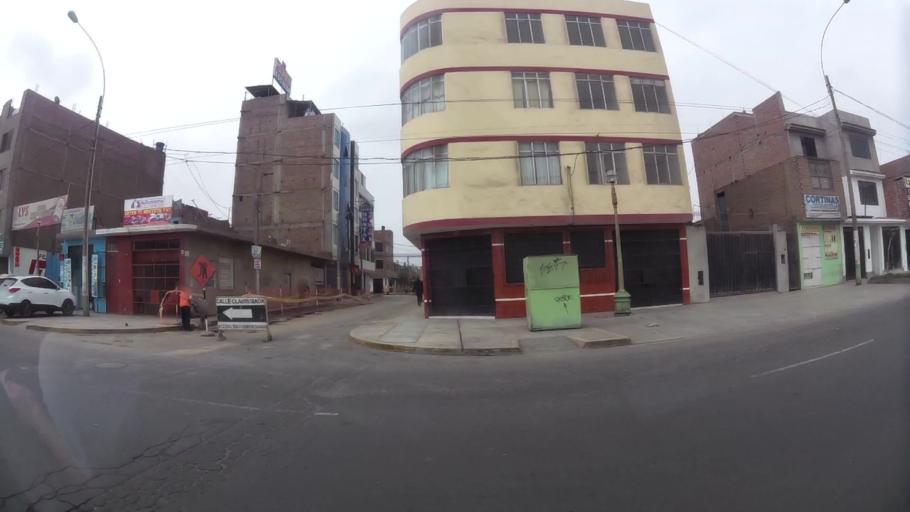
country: PE
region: Callao
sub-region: Callao
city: Callao
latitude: -11.9994
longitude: -77.1112
